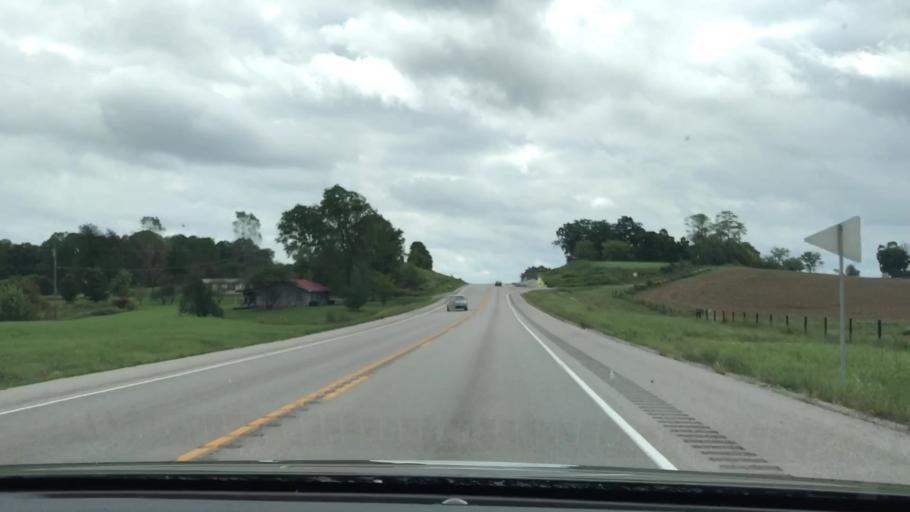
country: US
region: Kentucky
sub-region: Barren County
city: Glasgow
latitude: 36.9514
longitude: -85.8499
